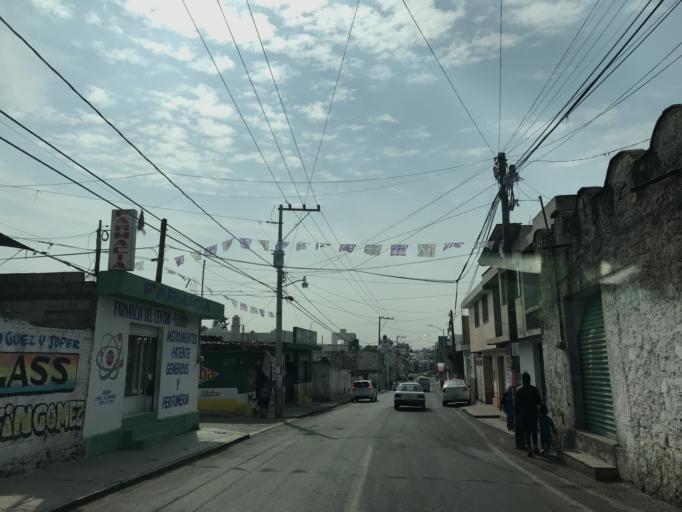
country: MX
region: Tlaxcala
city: Tenancingo
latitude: 19.1477
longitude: -98.2008
